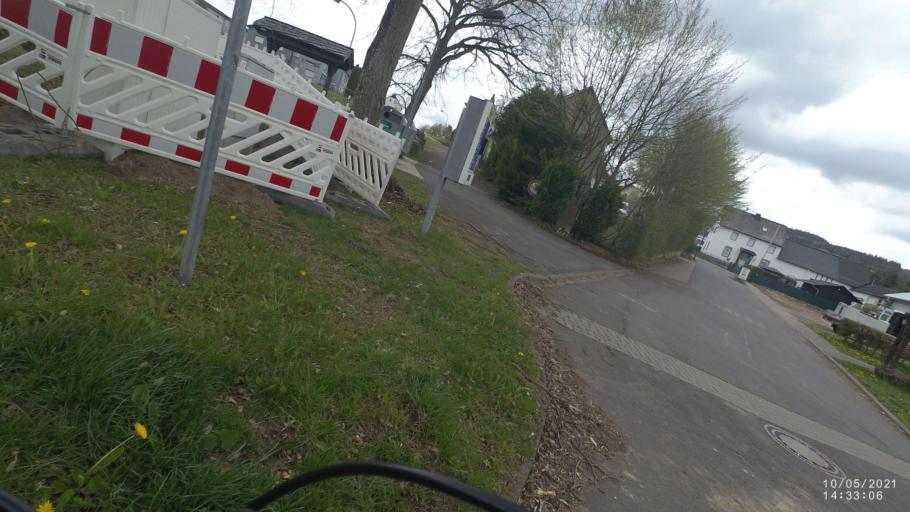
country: DE
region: Rheinland-Pfalz
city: Nitz
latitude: 50.3495
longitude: 7.0316
